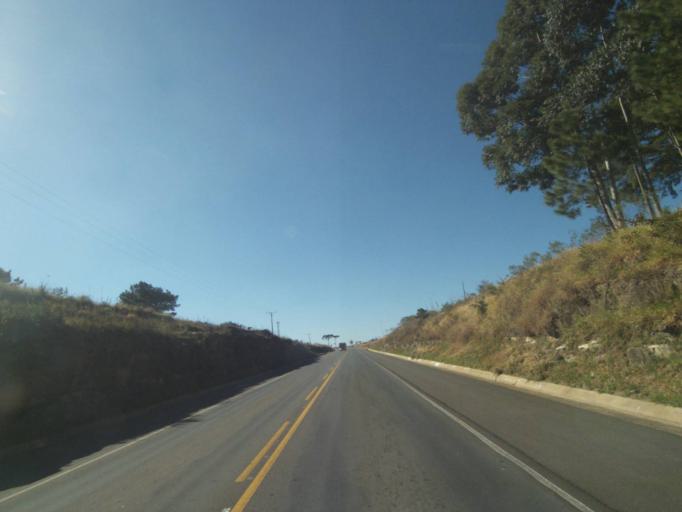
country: BR
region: Parana
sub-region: Tibagi
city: Tibagi
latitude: -24.8034
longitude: -50.4701
